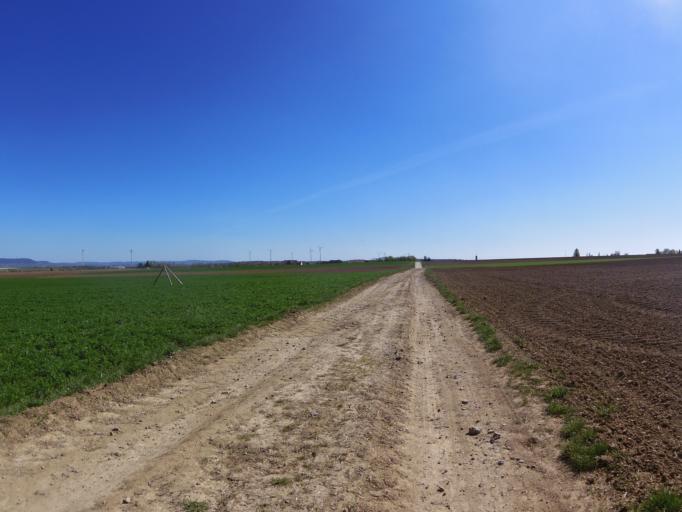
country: DE
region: Bavaria
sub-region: Regierungsbezirk Unterfranken
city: Biebelried
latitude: 49.8041
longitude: 10.0859
